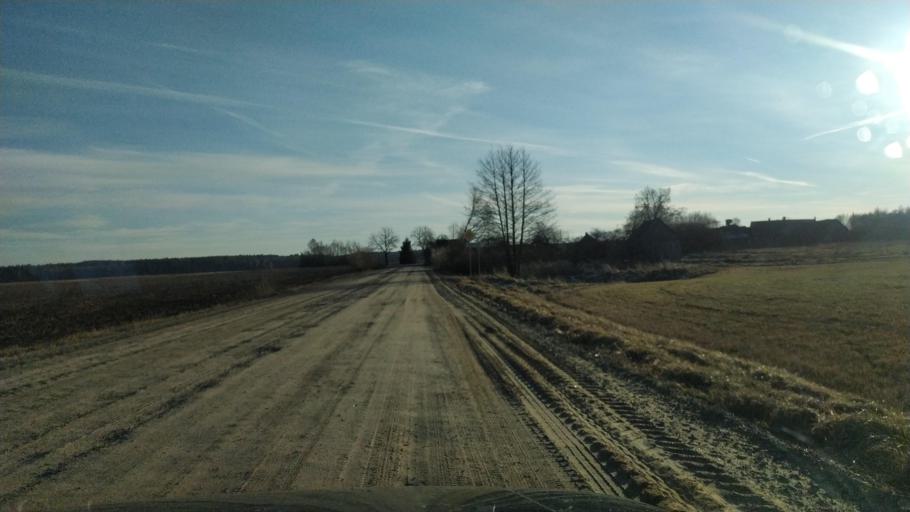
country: BY
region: Brest
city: Pruzhany
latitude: 52.5524
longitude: 24.2951
